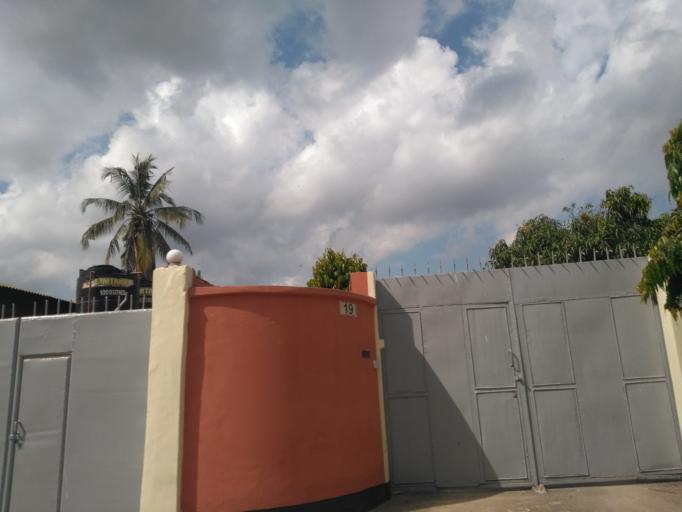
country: TZ
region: Dar es Salaam
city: Magomeni
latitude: -6.7643
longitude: 39.2465
